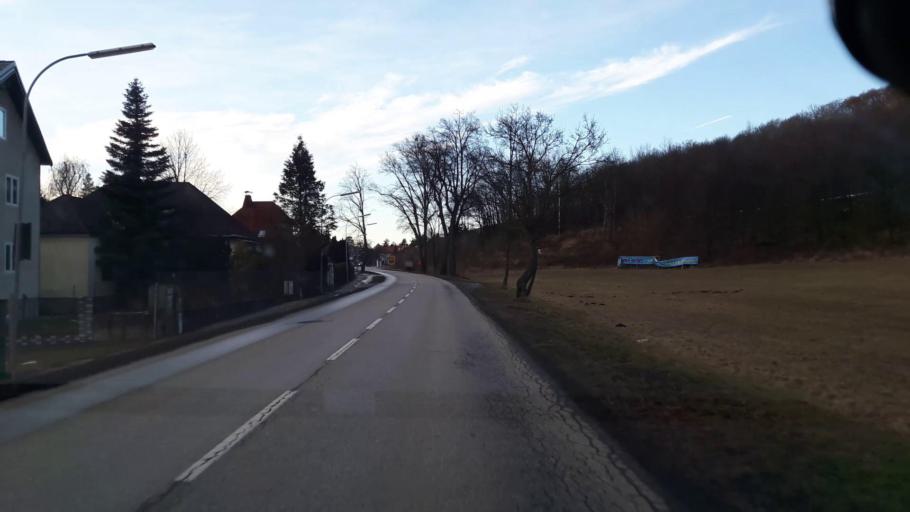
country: AT
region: Lower Austria
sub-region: Politischer Bezirk Wien-Umgebung
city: Mauerbach
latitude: 48.2321
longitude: 16.1967
